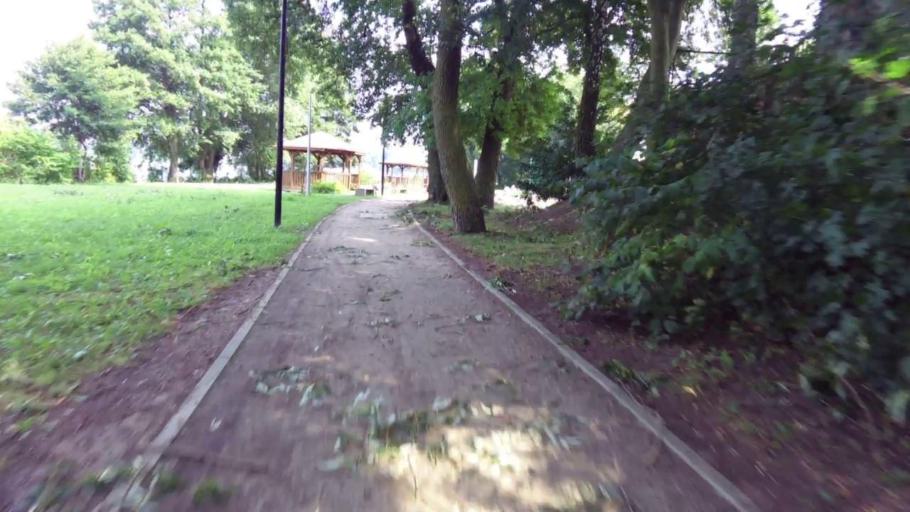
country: PL
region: West Pomeranian Voivodeship
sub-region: Powiat choszczenski
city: Choszczno
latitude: 53.1587
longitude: 15.4155
